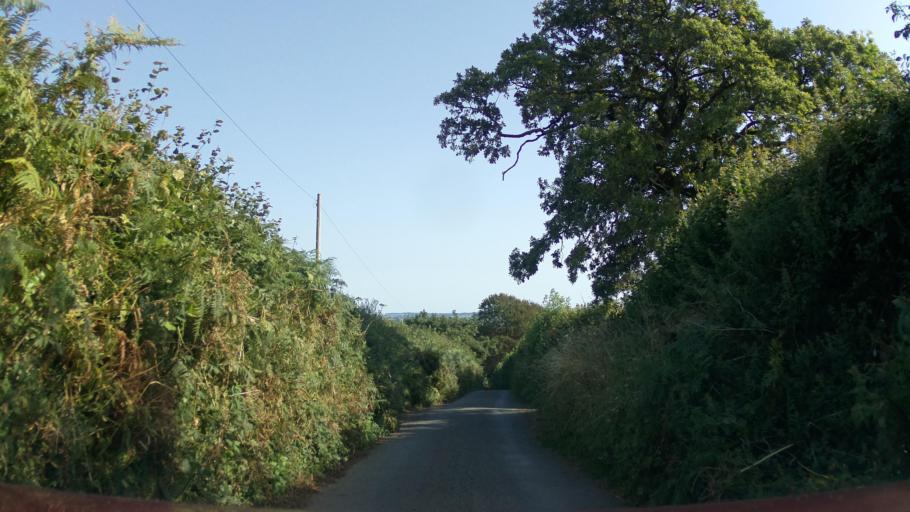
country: GB
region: England
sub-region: Devon
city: Totnes
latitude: 50.4221
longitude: -3.7239
